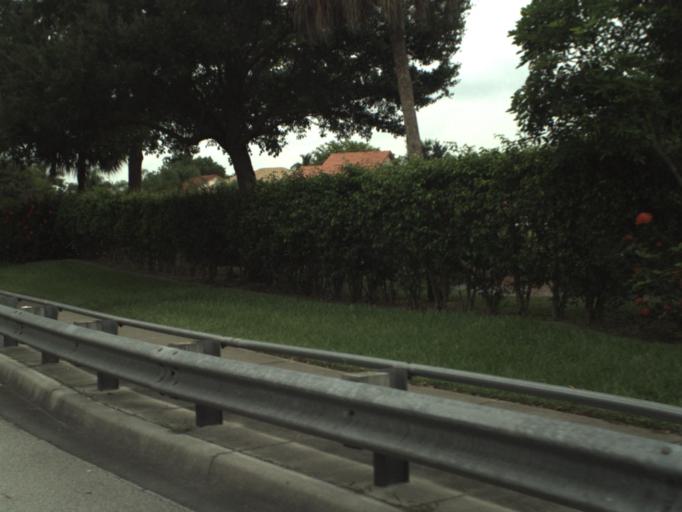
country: US
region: Florida
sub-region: Broward County
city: Plantation
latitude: 26.1469
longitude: -80.2764
